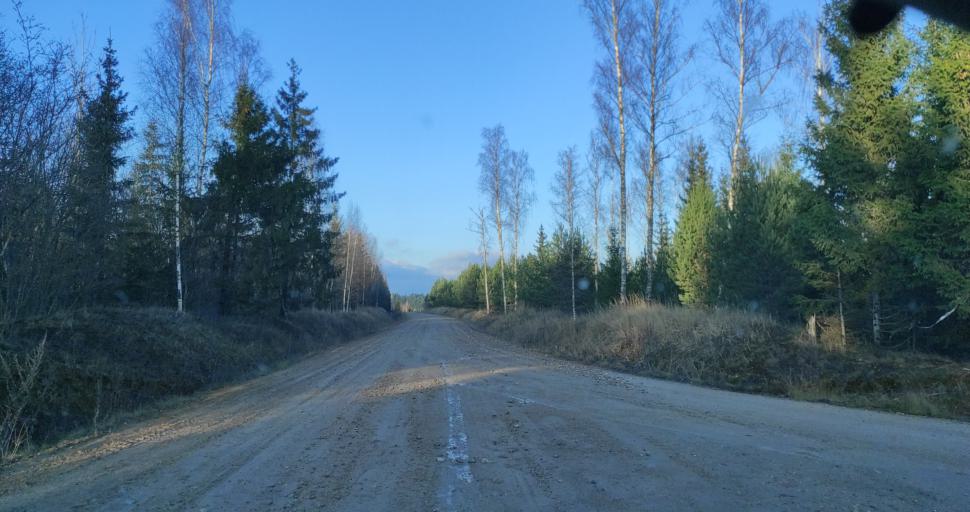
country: LV
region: Kuldigas Rajons
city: Kuldiga
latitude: 57.0546
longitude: 21.8670
